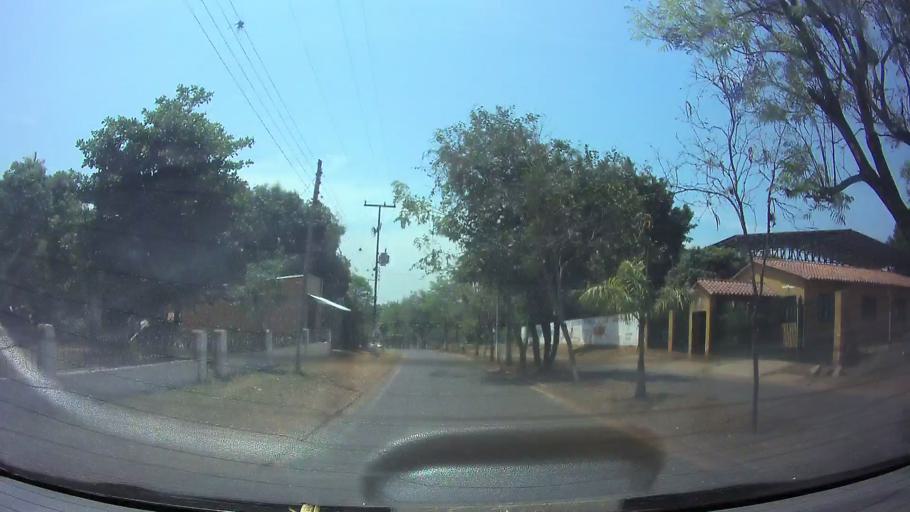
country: PY
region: Central
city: Ita
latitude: -25.4281
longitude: -57.3959
